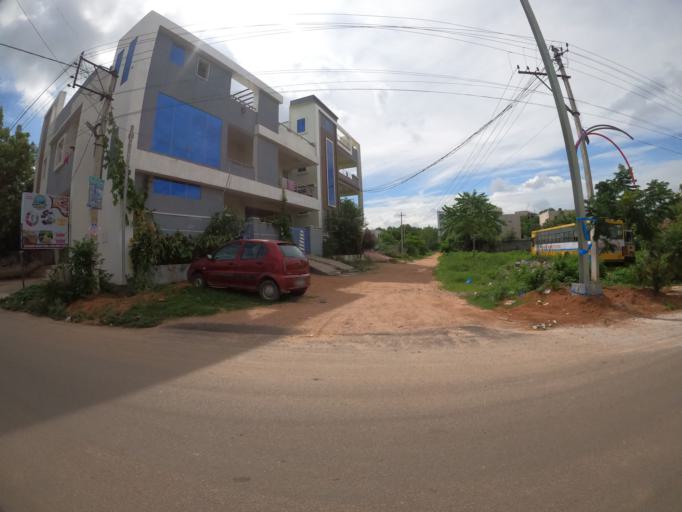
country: IN
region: Telangana
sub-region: Hyderabad
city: Hyderabad
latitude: 17.3528
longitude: 78.3881
